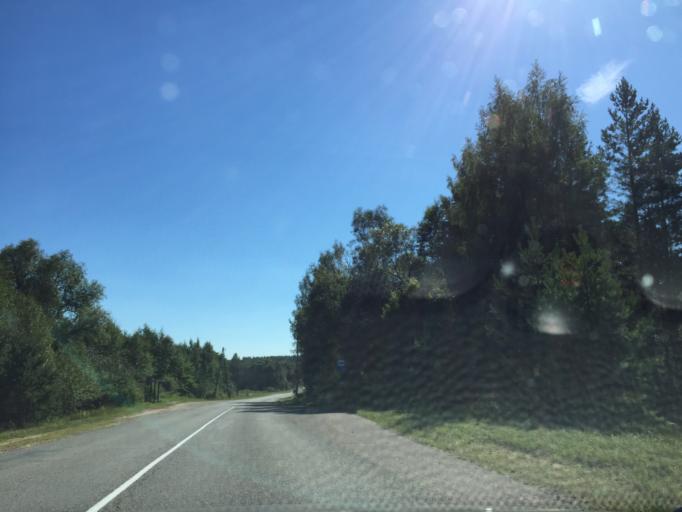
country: LV
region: Akniste
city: Akniste
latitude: 56.1272
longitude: 25.8310
